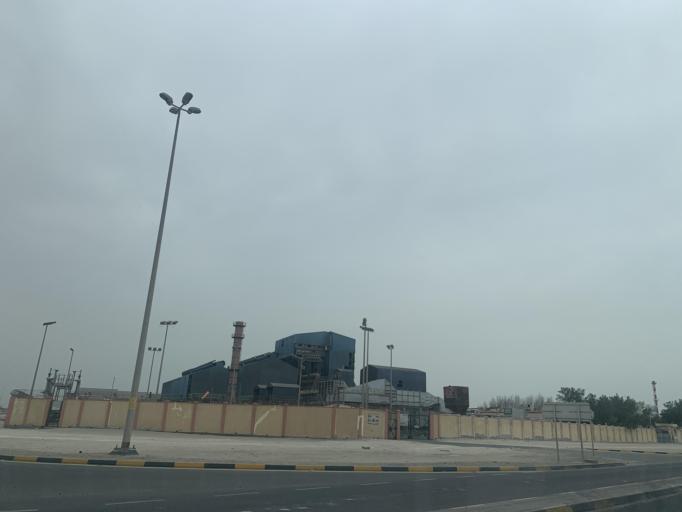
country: BH
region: Muharraq
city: Al Hadd
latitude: 26.2089
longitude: 50.6722
